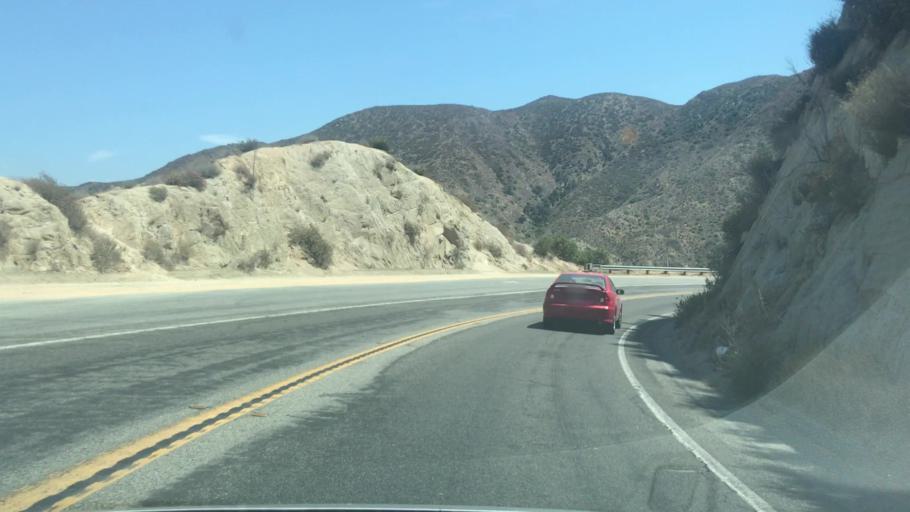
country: US
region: California
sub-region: Riverside County
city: Lakeland Village
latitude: 33.6483
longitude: -117.3846
